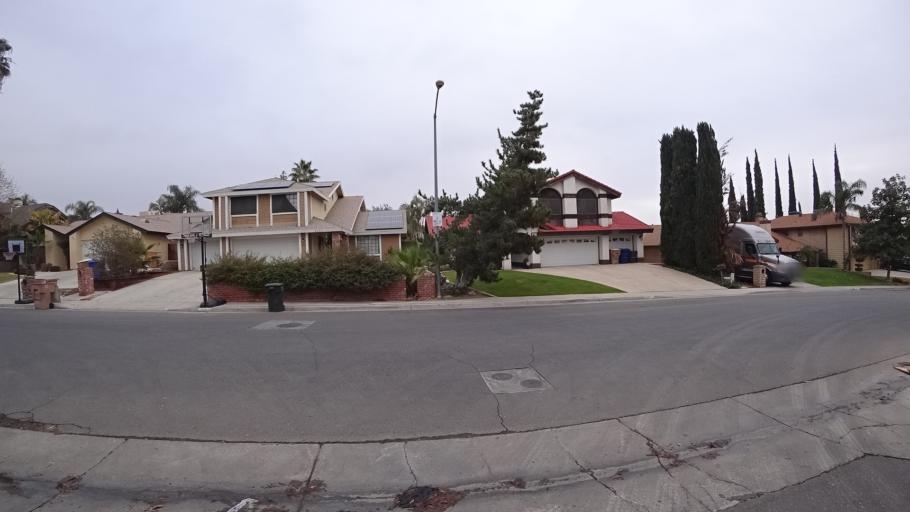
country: US
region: California
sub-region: Kern County
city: Bakersfield
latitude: 35.3813
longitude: -118.9365
